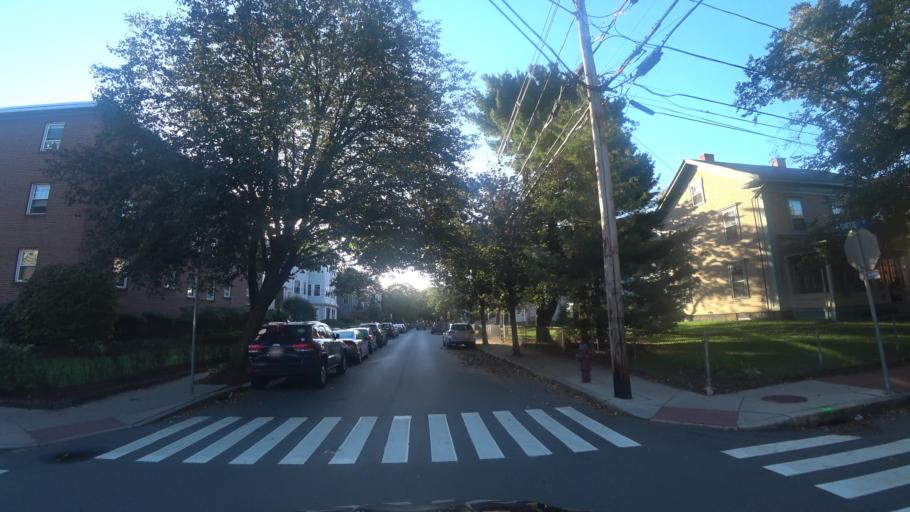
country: US
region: Massachusetts
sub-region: Middlesex County
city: Somerville
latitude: 42.3942
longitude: -71.1240
